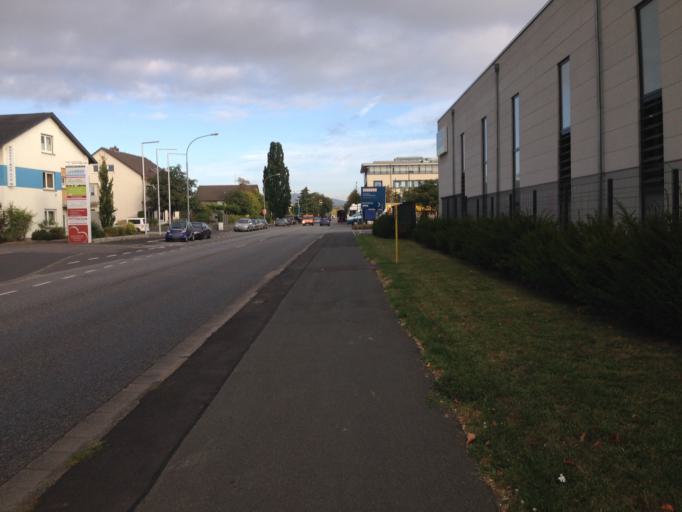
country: DE
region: Hesse
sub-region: Regierungsbezirk Giessen
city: Heuchelheim
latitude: 50.5942
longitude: 8.6307
